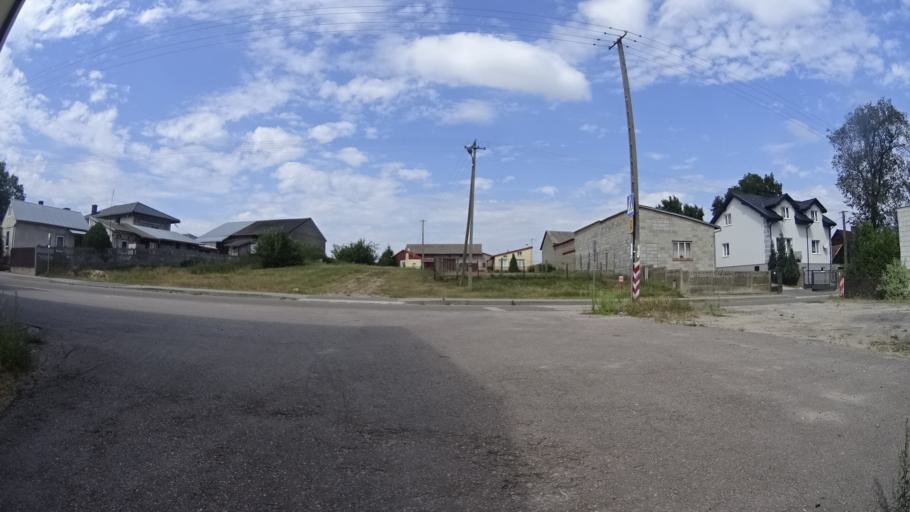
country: PL
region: Masovian Voivodeship
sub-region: Powiat bialobrzeski
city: Wysmierzyce
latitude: 51.6519
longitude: 20.8057
